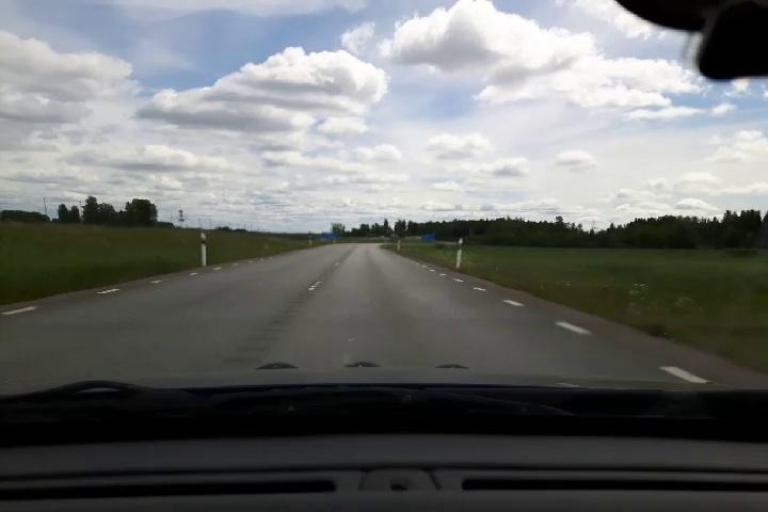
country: SE
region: Uppsala
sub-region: Tierps Kommun
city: Tierp
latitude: 60.3441
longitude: 17.4791
